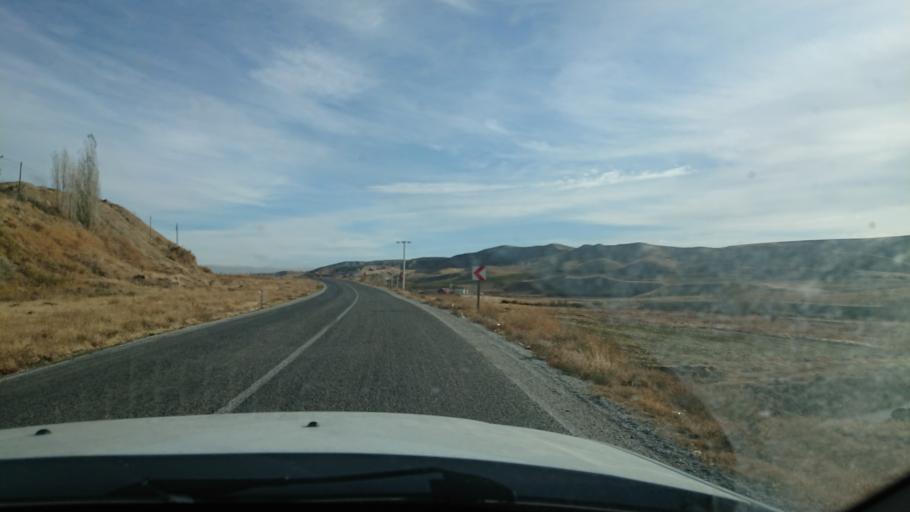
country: TR
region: Aksaray
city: Acipinar
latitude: 38.4856
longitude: 33.9153
